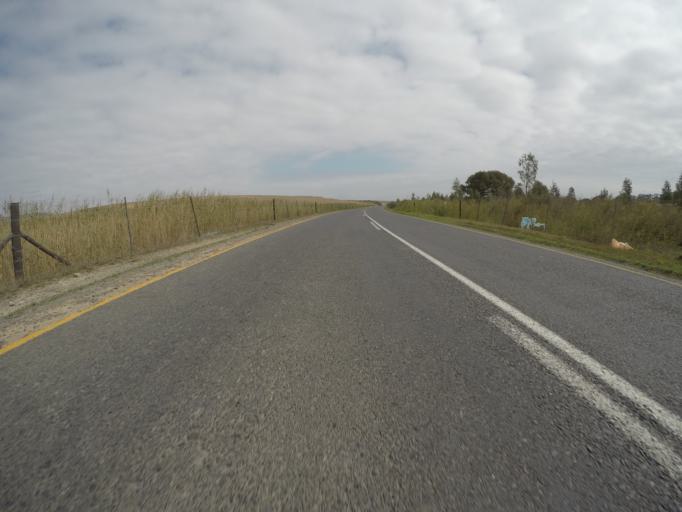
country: ZA
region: Western Cape
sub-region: City of Cape Town
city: Sunset Beach
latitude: -33.7879
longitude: 18.5545
